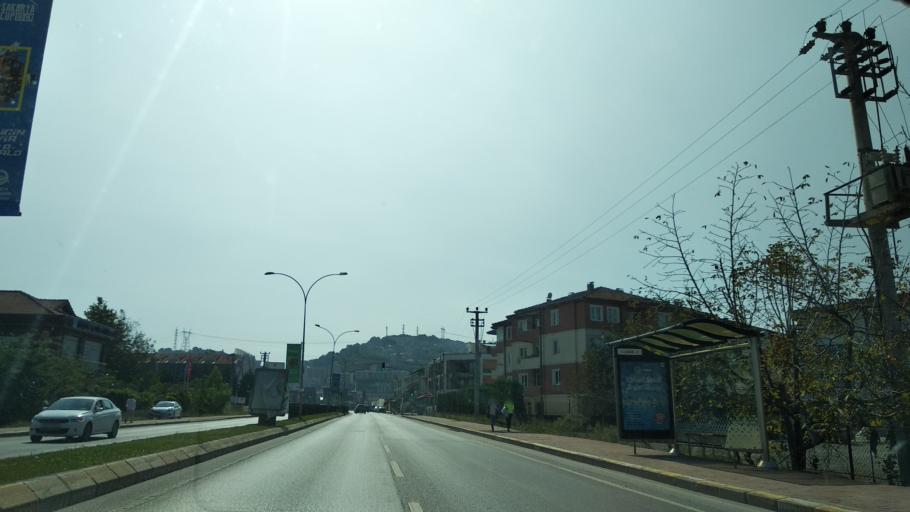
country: TR
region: Sakarya
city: Adapazari
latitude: 40.7634
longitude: 30.3632
